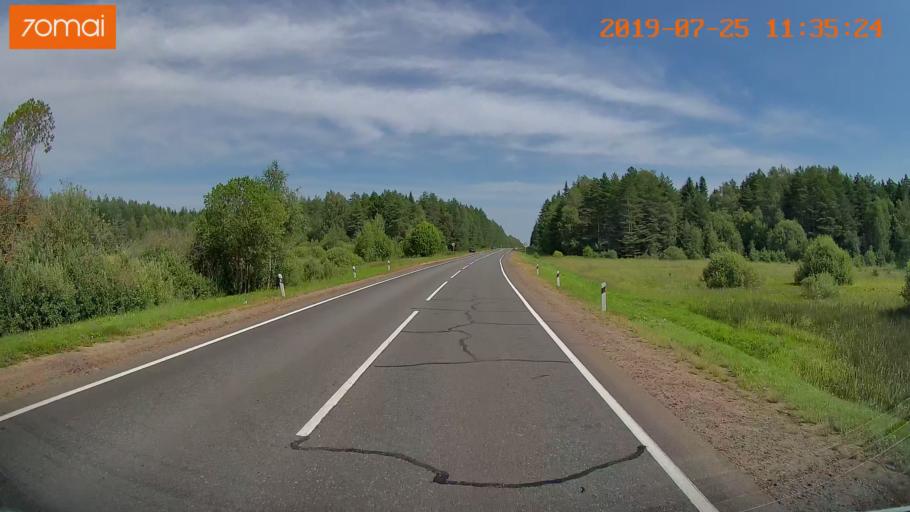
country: RU
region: Ivanovo
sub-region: Privolzhskiy Rayon
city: Ples
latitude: 57.4118
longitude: 41.4286
